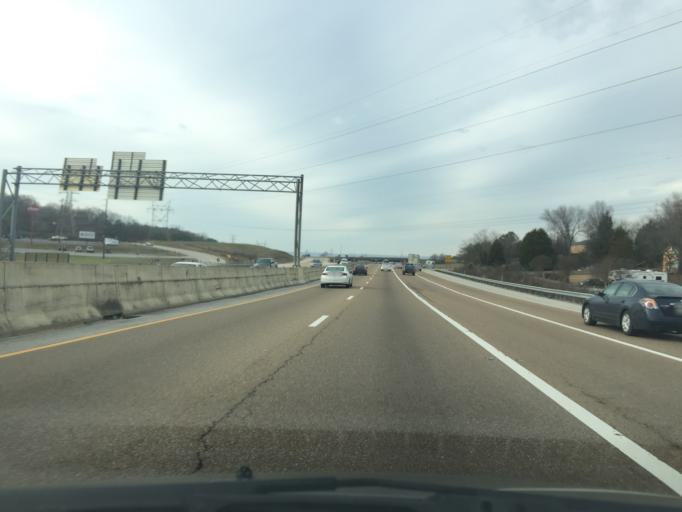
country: US
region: Tennessee
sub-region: Hamilton County
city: East Chattanooga
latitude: 35.0877
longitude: -85.2143
